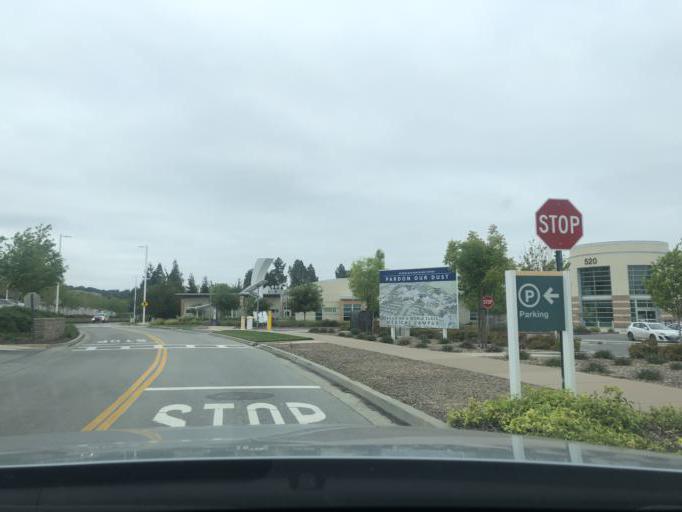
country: US
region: California
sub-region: Santa Clara County
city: Los Altos Hills
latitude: 37.4041
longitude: -122.1422
